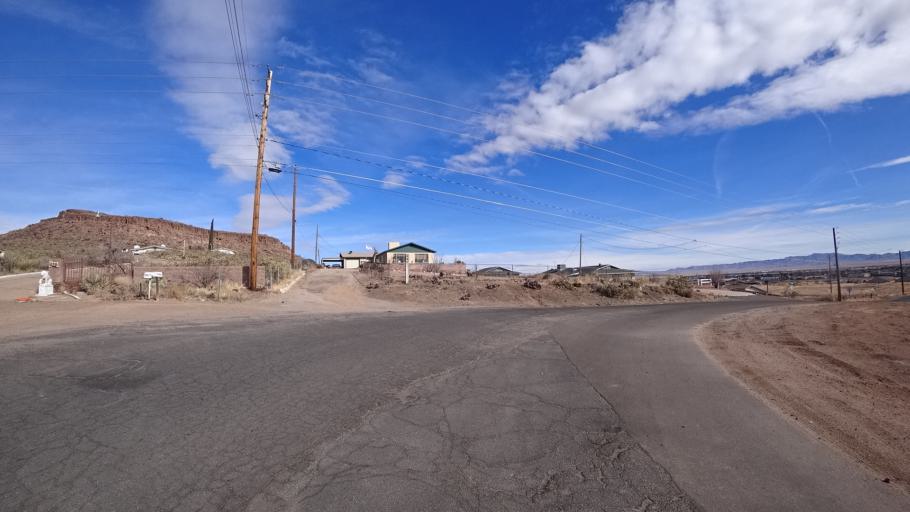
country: US
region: Arizona
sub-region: Mohave County
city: Kingman
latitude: 35.2218
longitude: -114.0492
